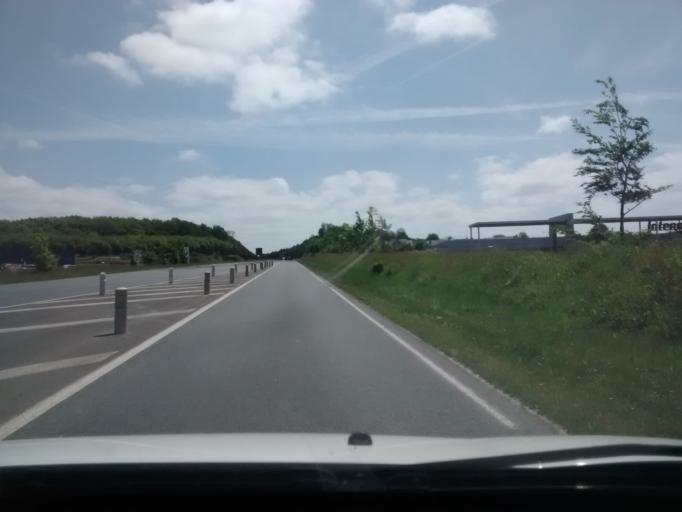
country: FR
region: Brittany
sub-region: Departement des Cotes-d'Armor
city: Lannion
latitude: 48.7333
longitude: -3.4364
